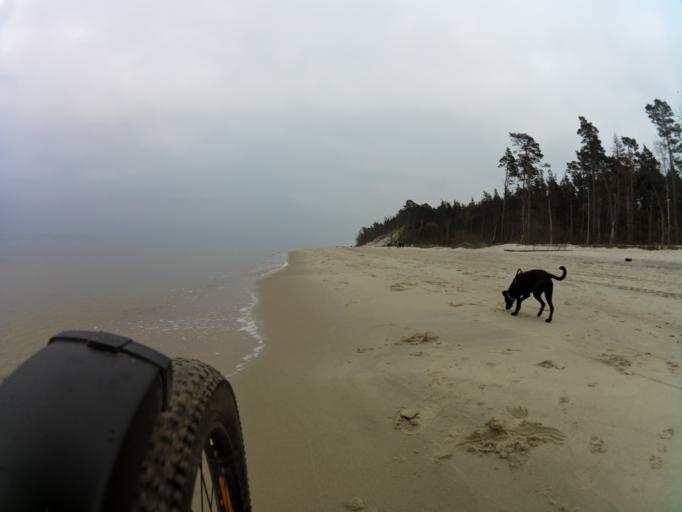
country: PL
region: Pomeranian Voivodeship
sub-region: Powiat pucki
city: Krokowa
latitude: 54.8320
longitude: 18.1396
